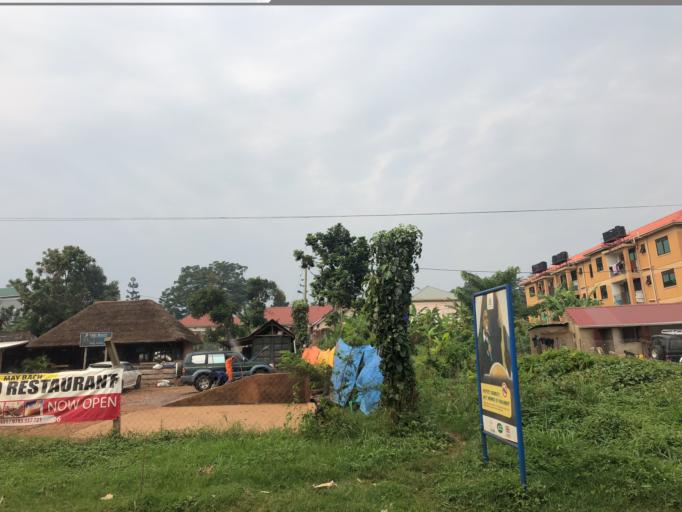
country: UG
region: Central Region
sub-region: Mukono District
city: Mukono
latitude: 0.3645
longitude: 32.7422
